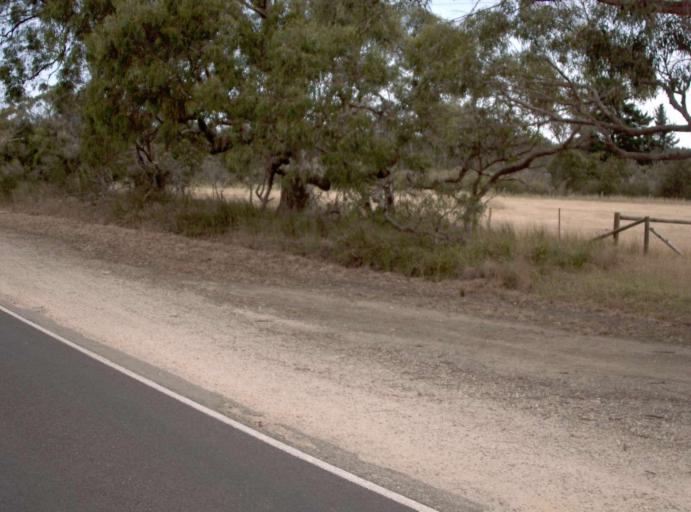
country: AU
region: Victoria
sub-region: Wellington
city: Sale
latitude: -38.2122
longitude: 147.1032
